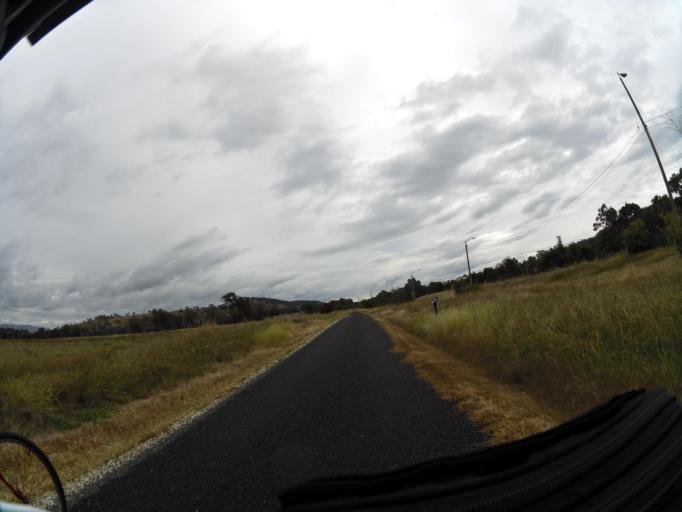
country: AU
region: Victoria
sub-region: Wodonga
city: Wodonga
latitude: -36.1502
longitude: 146.9409
